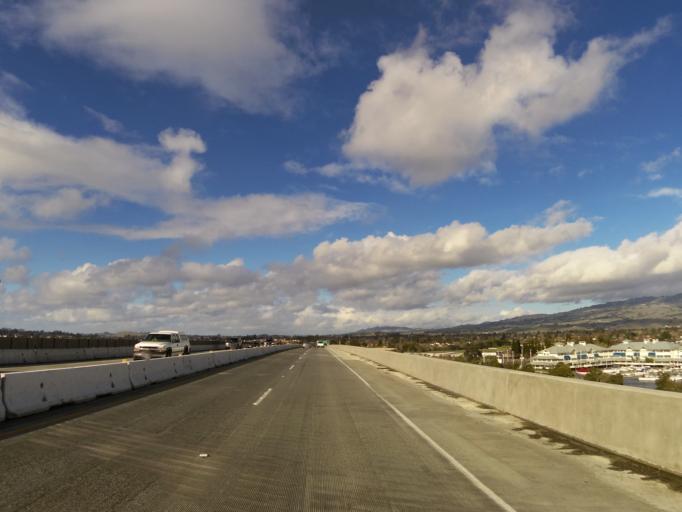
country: US
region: California
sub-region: Sonoma County
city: Petaluma
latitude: 38.2278
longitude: -122.6150
